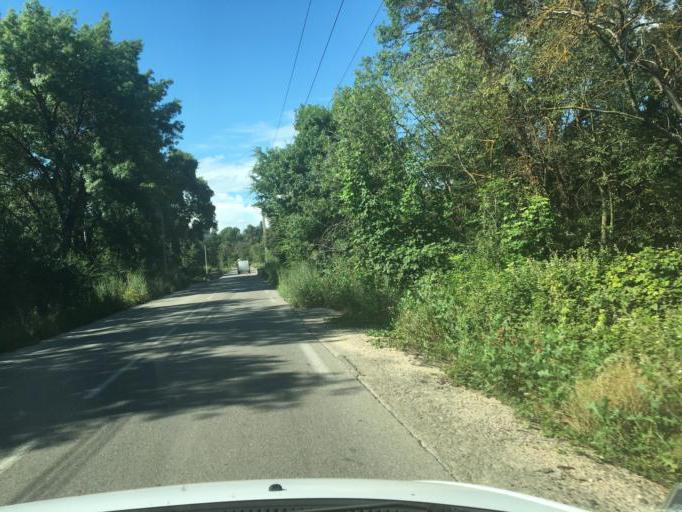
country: FR
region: Provence-Alpes-Cote d'Azur
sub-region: Departement des Bouches-du-Rhone
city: Eguilles
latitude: 43.5267
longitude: 5.3517
